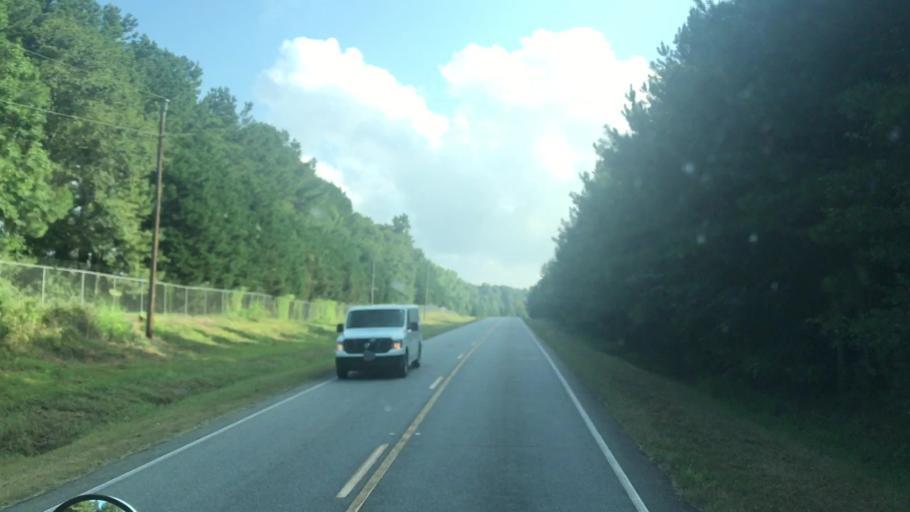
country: US
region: Florida
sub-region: Gadsden County
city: Havana
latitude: 30.7268
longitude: -84.4865
